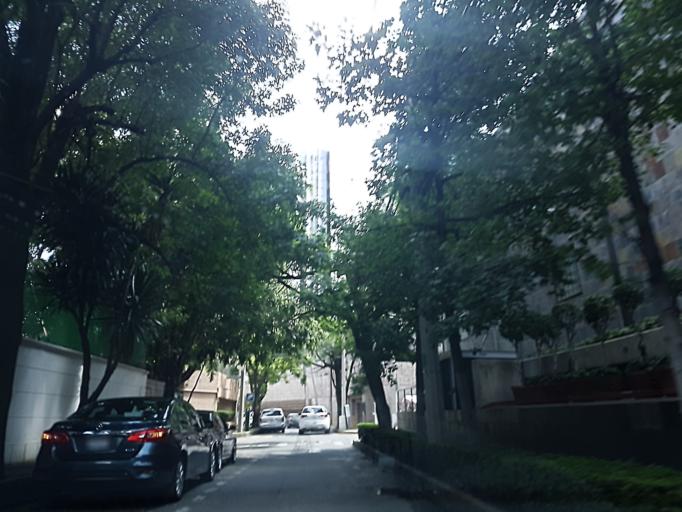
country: MX
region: Mexico City
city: Alvaro Obregon
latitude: 19.3537
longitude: -99.1848
